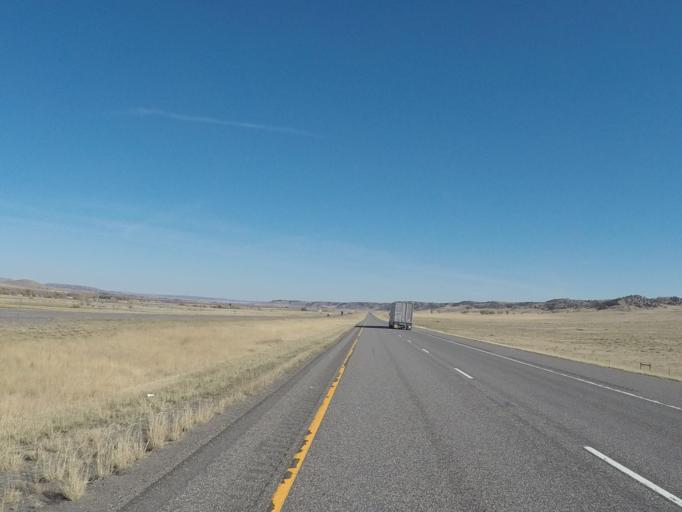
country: US
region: Montana
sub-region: Sweet Grass County
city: Big Timber
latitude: 45.7513
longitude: -110.1564
